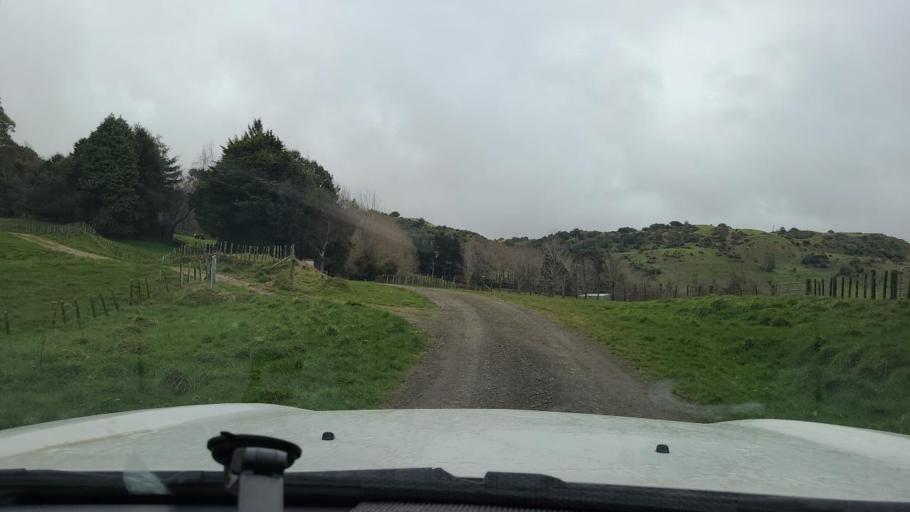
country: NZ
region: Hawke's Bay
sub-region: Wairoa District
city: Wairoa
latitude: -38.5420
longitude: 177.4112
